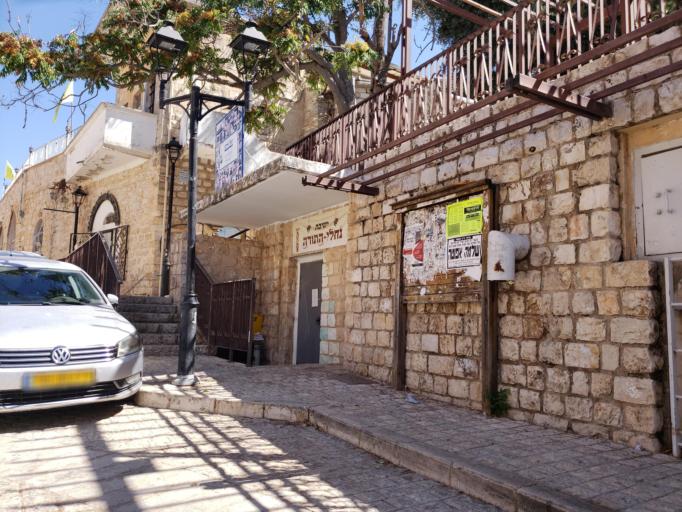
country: IL
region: Northern District
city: Safed
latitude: 32.9647
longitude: 35.4943
